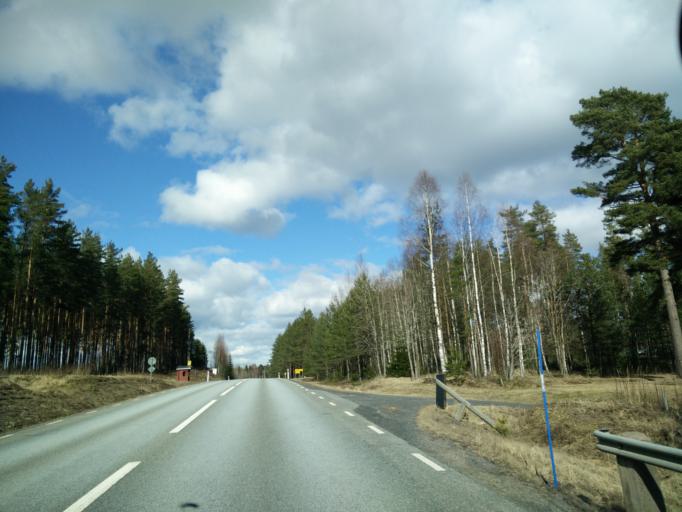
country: SE
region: Vaermland
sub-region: Munkfors Kommun
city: Munkfors
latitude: 59.9176
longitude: 13.5718
